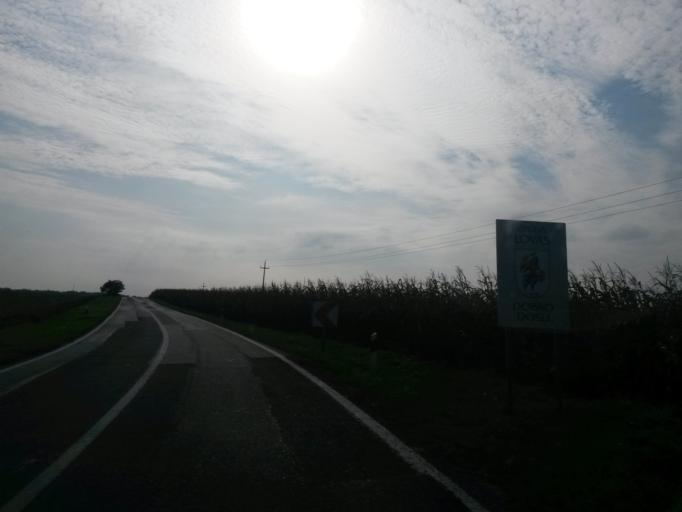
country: HR
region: Vukovarsko-Srijemska
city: Lovas
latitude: 45.2746
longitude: 19.1355
